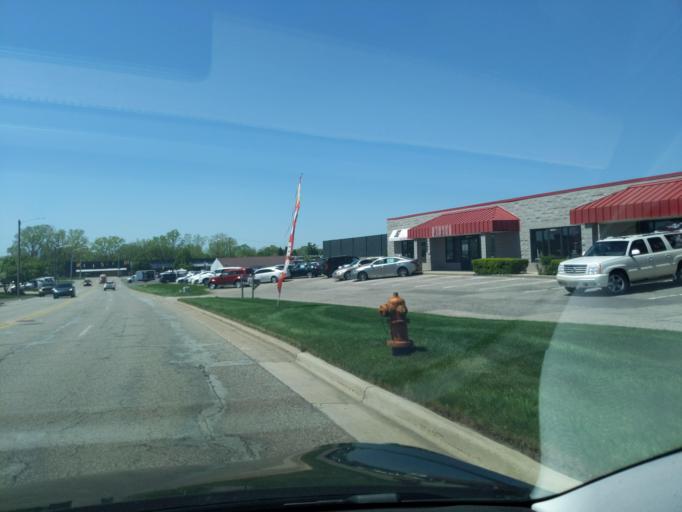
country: US
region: Michigan
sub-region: Kent County
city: East Grand Rapids
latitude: 42.9108
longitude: -85.6053
